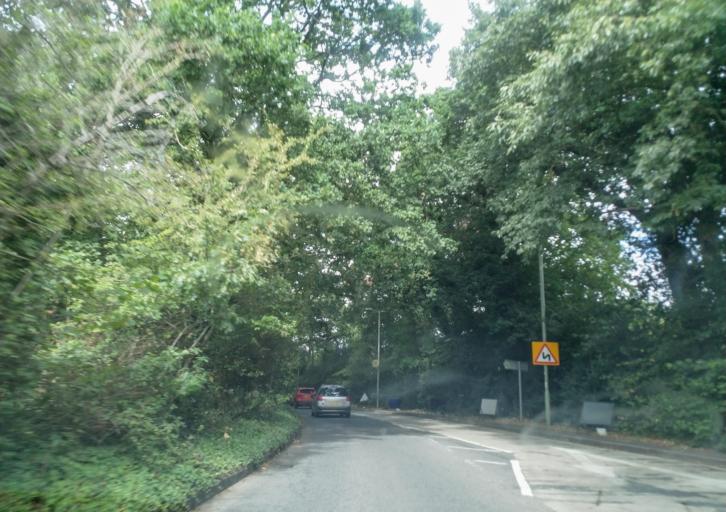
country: GB
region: England
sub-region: Bracknell Forest
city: Sandhurst
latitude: 51.3273
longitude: -0.7784
